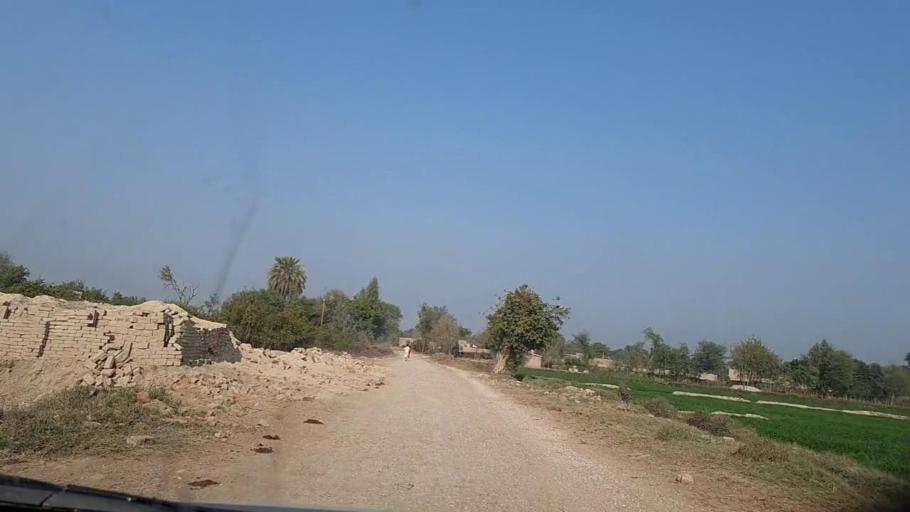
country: PK
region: Sindh
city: Moro
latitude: 26.8003
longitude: 67.9462
